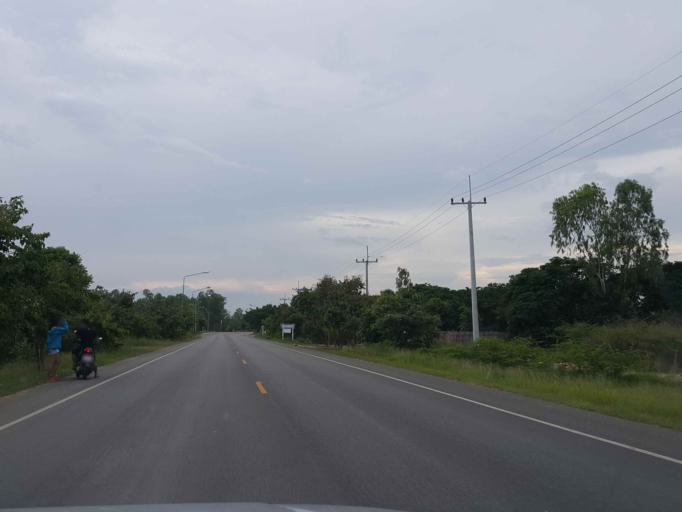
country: TH
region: Lampang
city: Ko Kha
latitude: 18.2280
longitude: 99.3925
